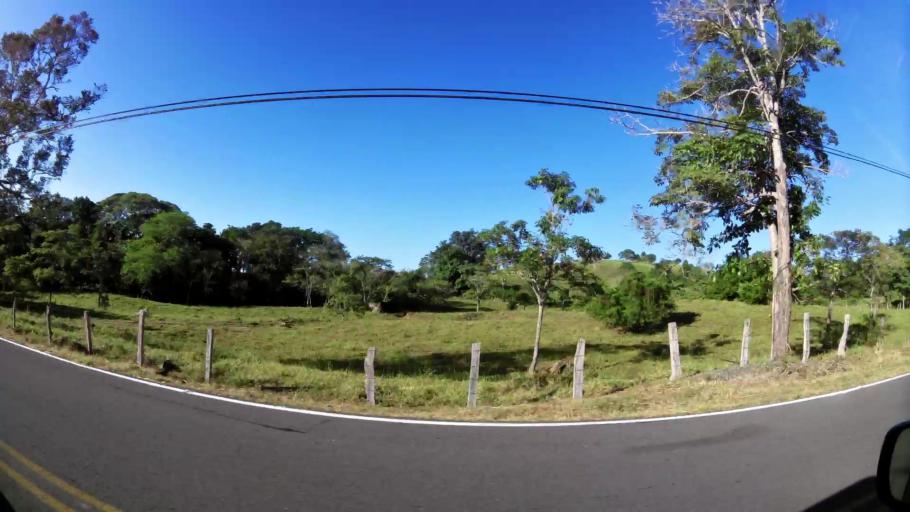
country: CR
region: Puntarenas
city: Miramar
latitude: 10.1618
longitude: -84.8544
